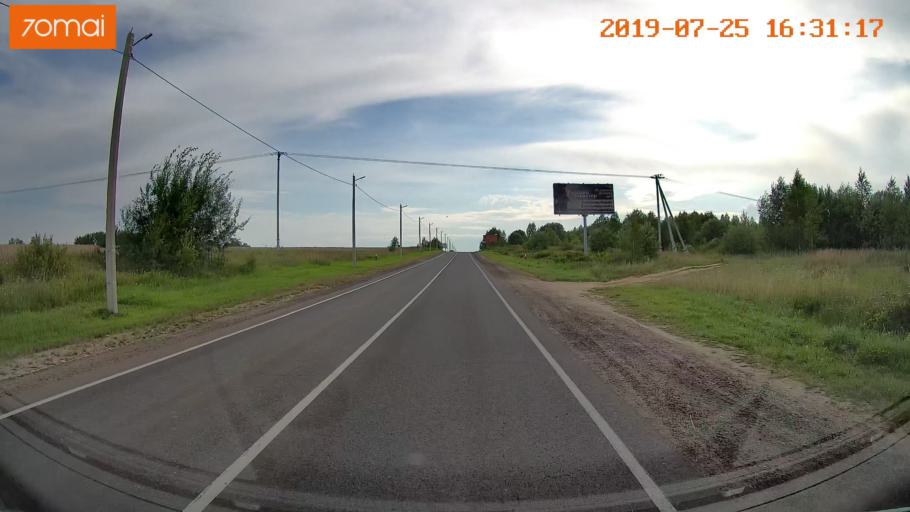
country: RU
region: Ivanovo
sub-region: Privolzhskiy Rayon
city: Ples
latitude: 57.4438
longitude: 41.4875
